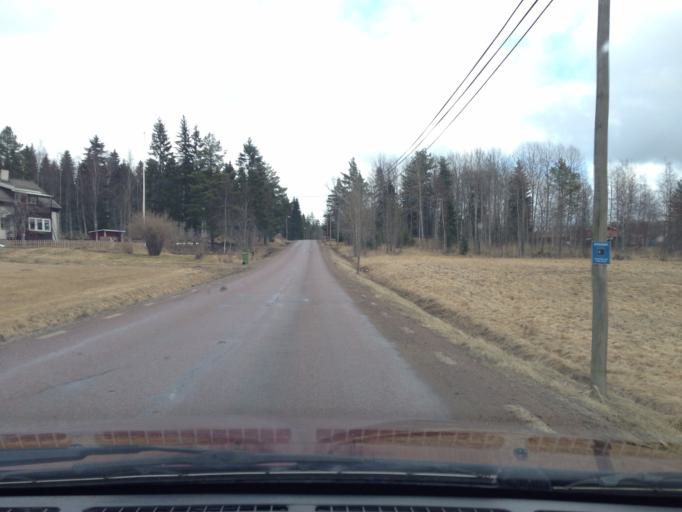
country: SE
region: Dalarna
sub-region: Smedjebackens Kommun
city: Smedjebacken
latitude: 60.1800
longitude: 15.3095
